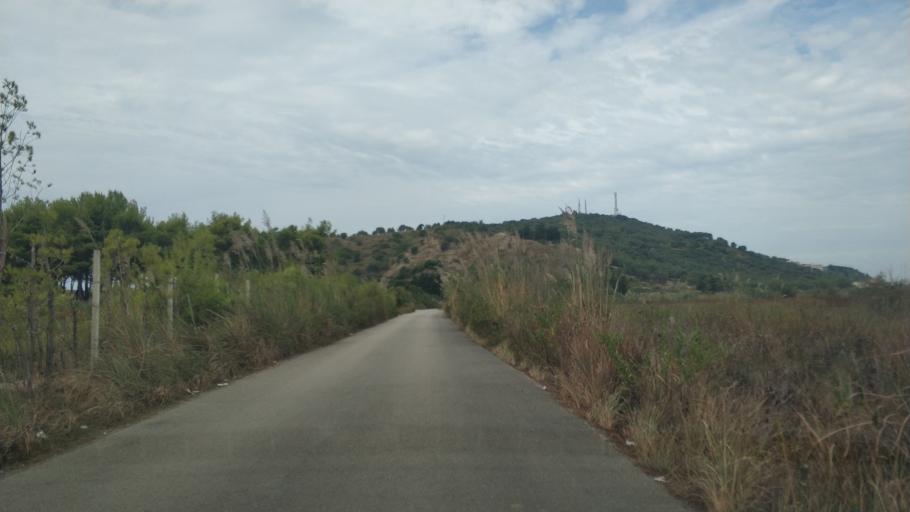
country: AL
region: Vlore
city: Vlore
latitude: 40.5047
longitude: 19.4247
